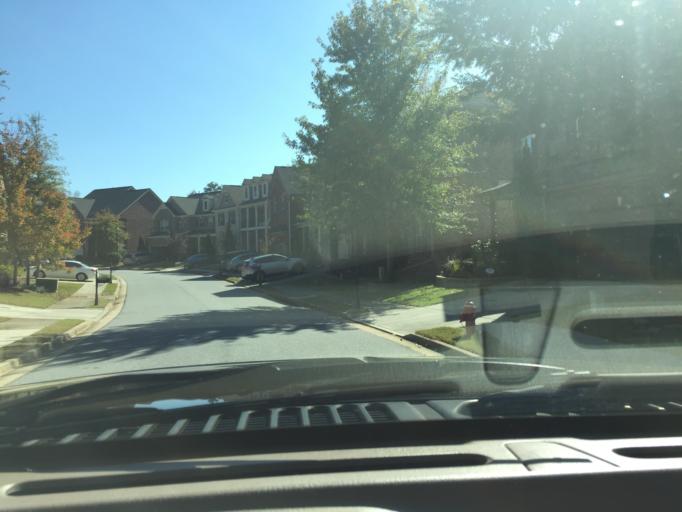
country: US
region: Georgia
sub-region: Fulton County
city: Johns Creek
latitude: 34.0546
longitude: -84.1597
